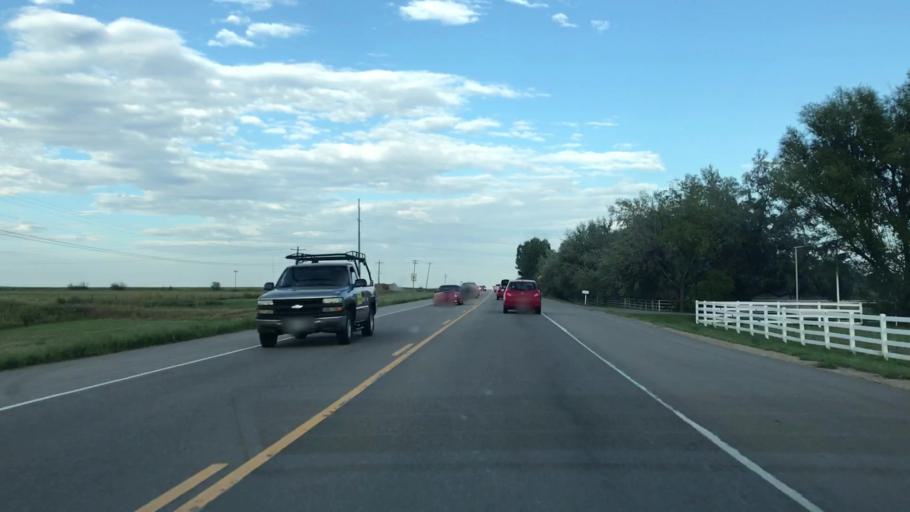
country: US
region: Colorado
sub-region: Weld County
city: Mead
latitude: 40.2038
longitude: -105.0405
